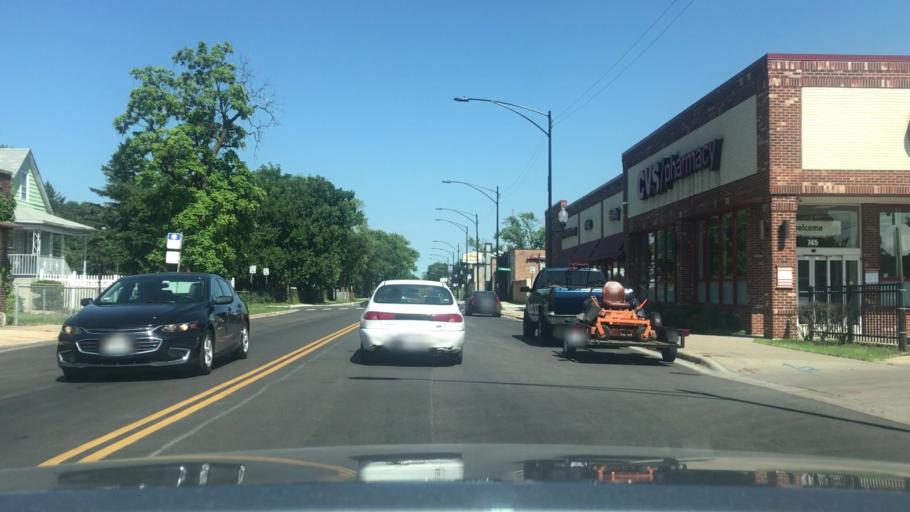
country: US
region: Illinois
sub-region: Cook County
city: Calumet Park
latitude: 41.7069
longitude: -87.6426
